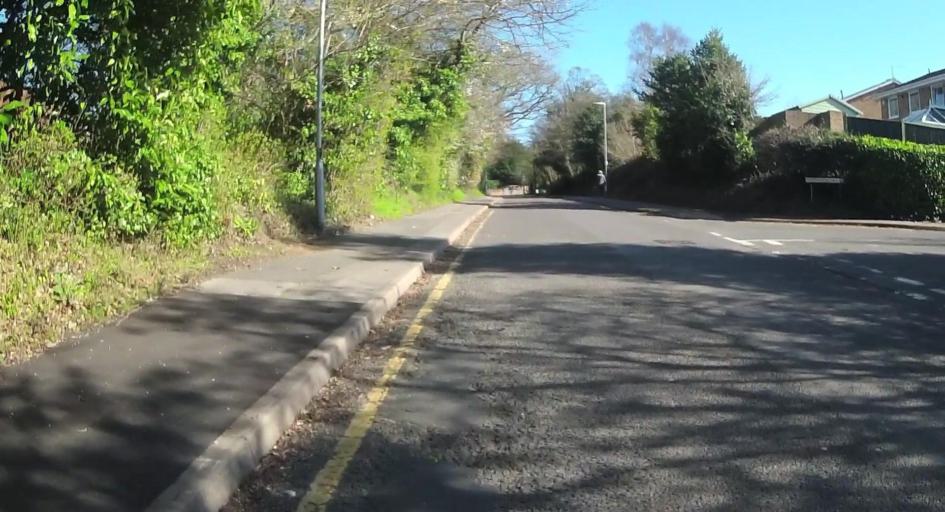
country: GB
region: England
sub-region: Bracknell Forest
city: Bracknell
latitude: 51.4216
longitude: -0.7460
